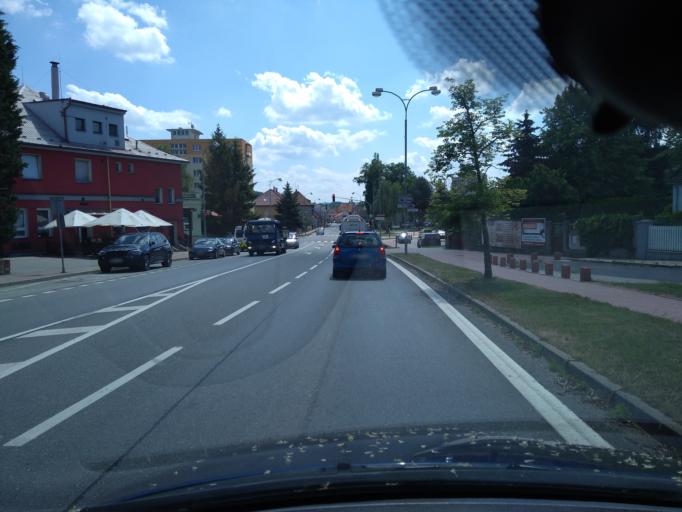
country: CZ
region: Plzensky
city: Prestice
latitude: 49.5768
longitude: 13.3297
